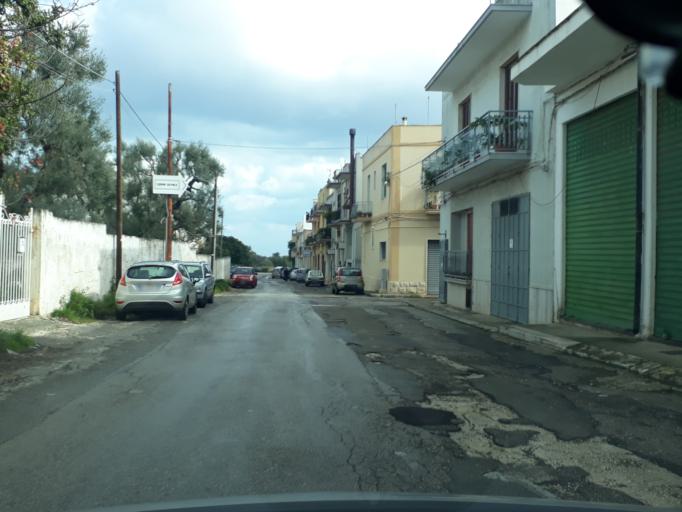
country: IT
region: Apulia
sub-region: Provincia di Brindisi
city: Fasano
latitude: 40.8415
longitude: 17.3589
